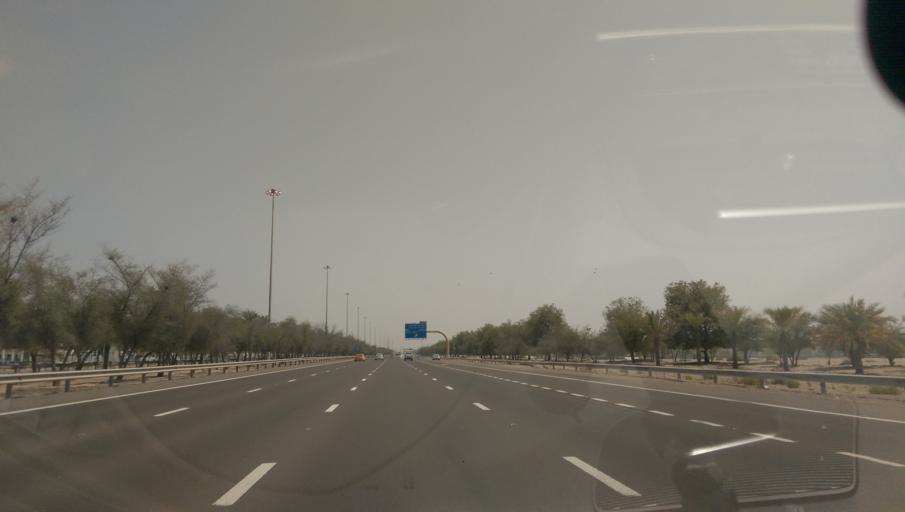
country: AE
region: Abu Dhabi
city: Abu Dhabi
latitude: 24.5255
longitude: 54.6919
